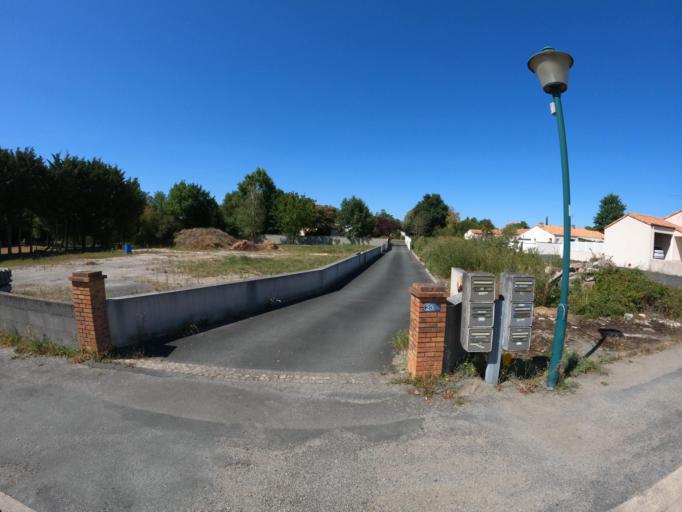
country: FR
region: Pays de la Loire
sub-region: Departement de la Vendee
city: La Boissiere-de-Montaigu
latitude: 46.9498
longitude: -1.1874
